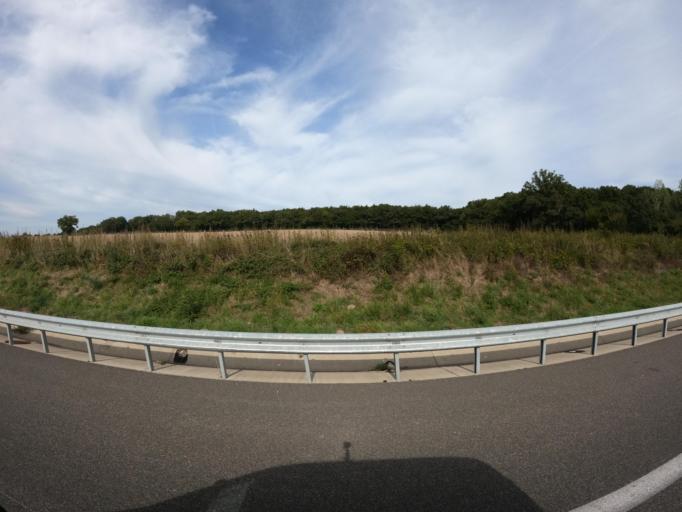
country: FR
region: Bourgogne
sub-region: Departement de Saone-et-Loire
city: Saint-Eusebe
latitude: 46.7099
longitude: 4.4264
